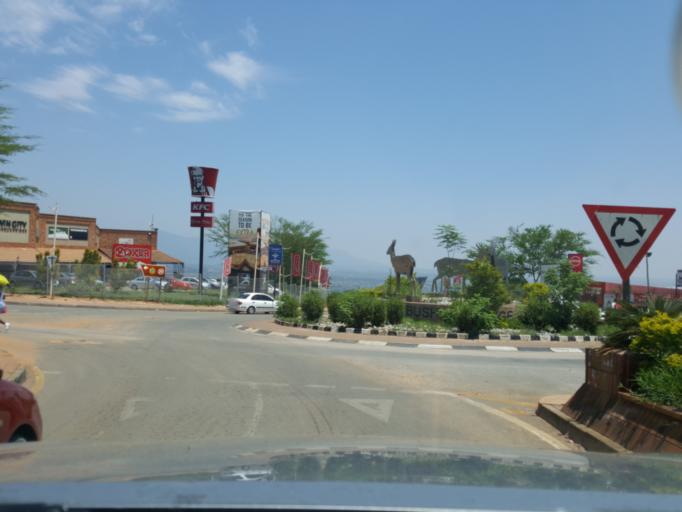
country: ZA
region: Limpopo
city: Thulamahashi
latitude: -24.8346
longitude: 31.0709
